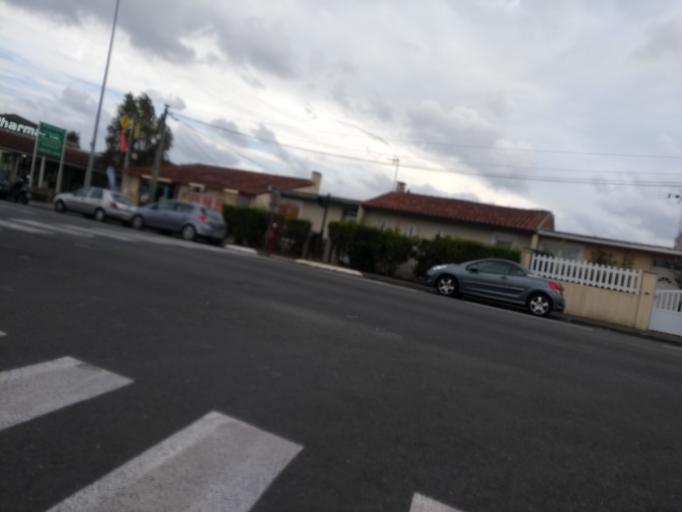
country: FR
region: Aquitaine
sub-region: Departement de la Gironde
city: Pessac
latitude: 44.8051
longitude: -0.6565
